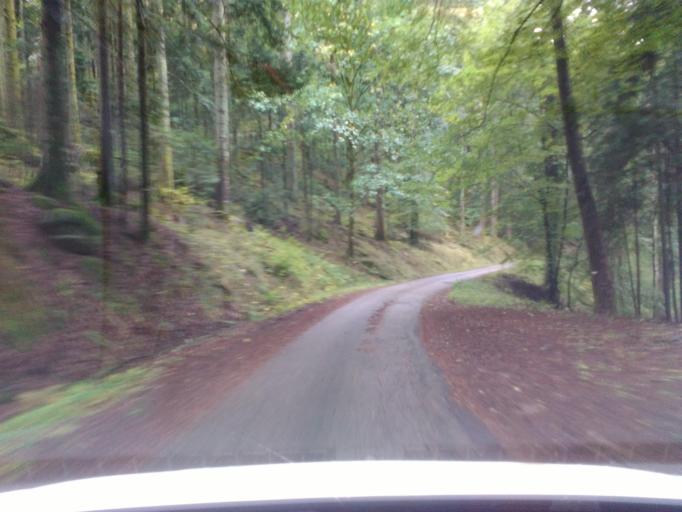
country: FR
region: Lorraine
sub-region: Departement des Vosges
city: Sainte-Marguerite
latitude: 48.3201
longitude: 7.0089
